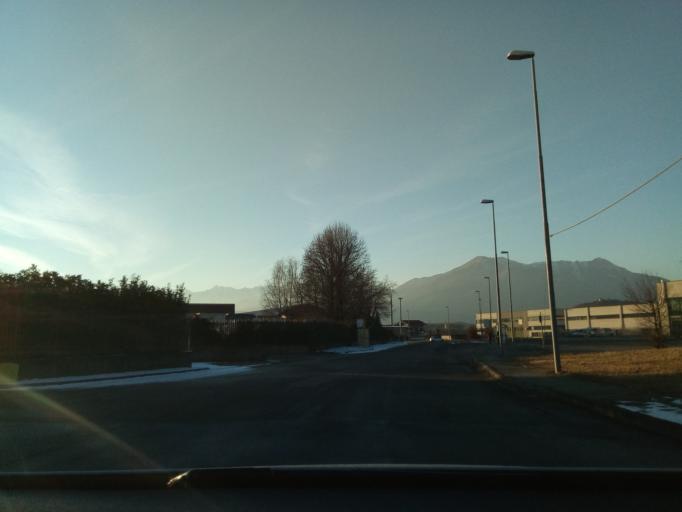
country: IT
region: Piedmont
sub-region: Provincia di Torino
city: Burolo
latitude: 45.4740
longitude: 7.9253
